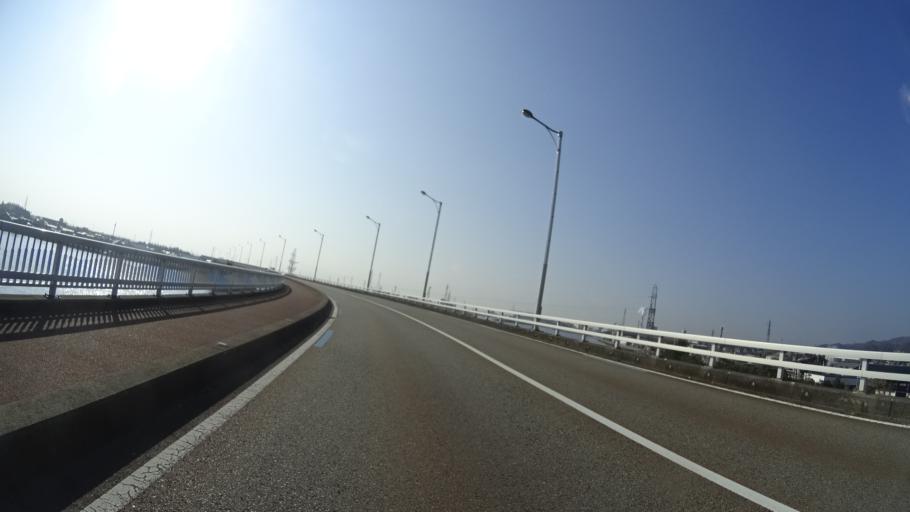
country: JP
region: Toyama
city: Nishishinminato
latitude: 36.7904
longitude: 137.0583
